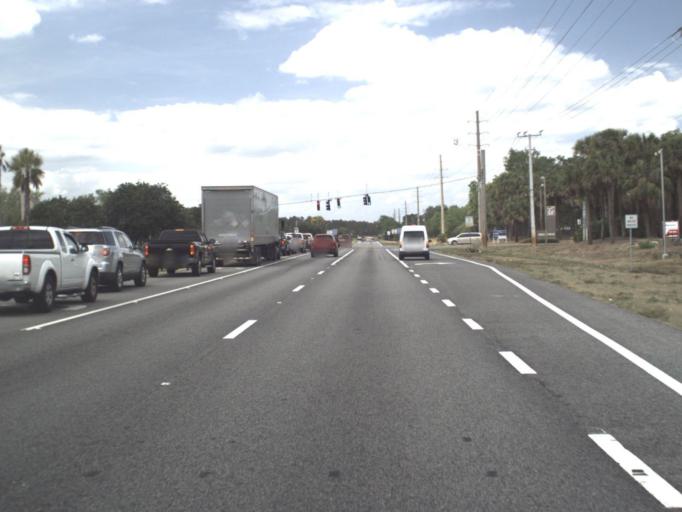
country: US
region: Florida
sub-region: Brevard County
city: Port Saint John
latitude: 28.5309
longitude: -80.8125
